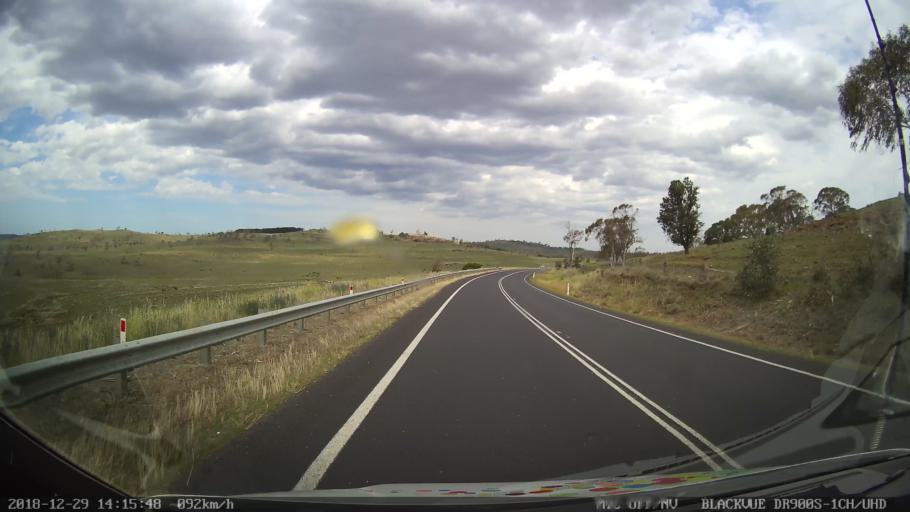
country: AU
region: New South Wales
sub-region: Cooma-Monaro
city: Cooma
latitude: -36.4601
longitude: 149.2437
